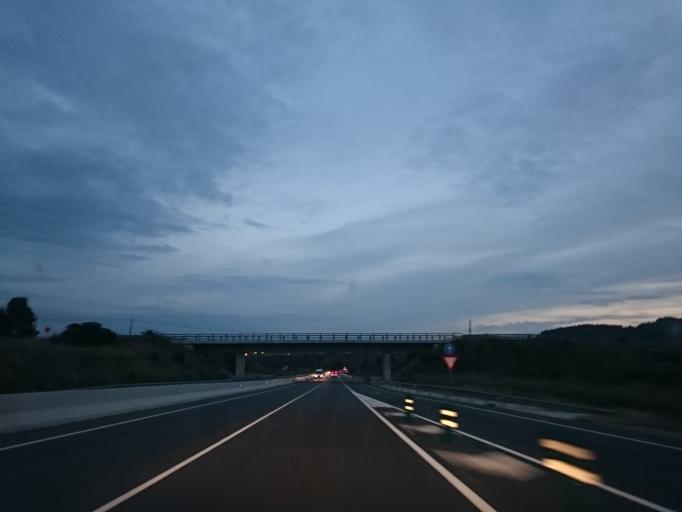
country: ES
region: Catalonia
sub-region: Provincia de Barcelona
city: el Pla del Penedes
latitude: 41.3994
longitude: 1.7065
